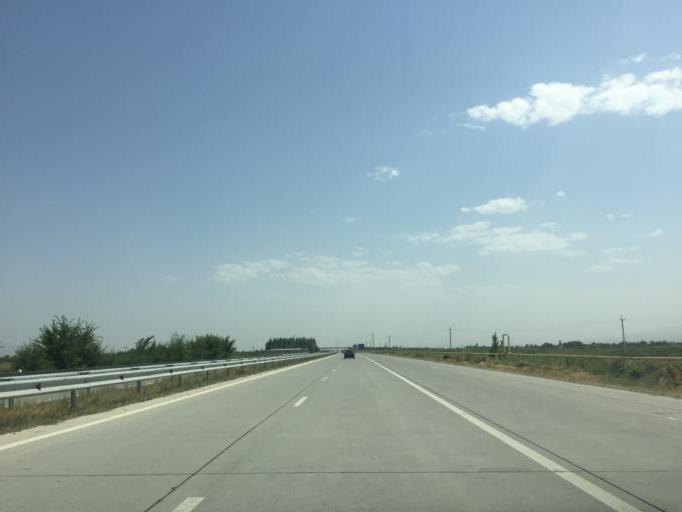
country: AM
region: Ararat
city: Mrgavet
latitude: 40.0127
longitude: 44.4697
